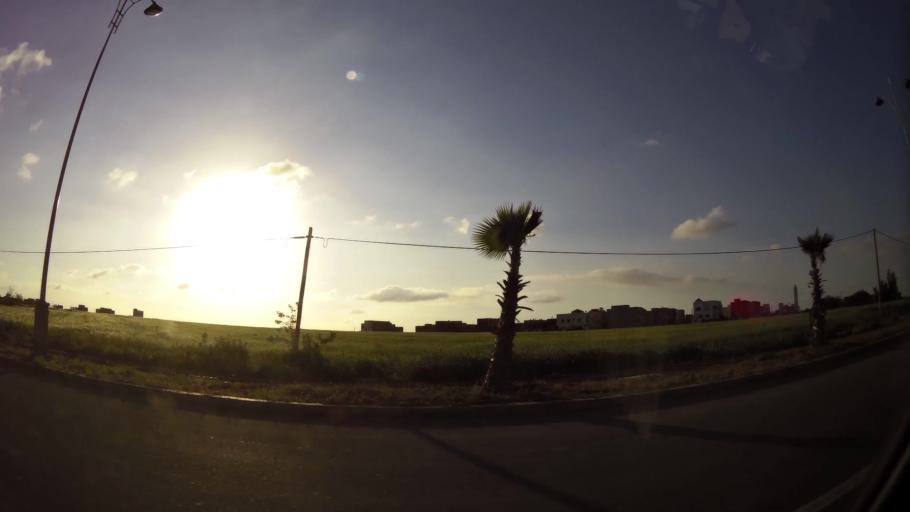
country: MA
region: Chaouia-Ouardigha
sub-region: Settat Province
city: Settat
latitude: 33.0068
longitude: -7.5945
